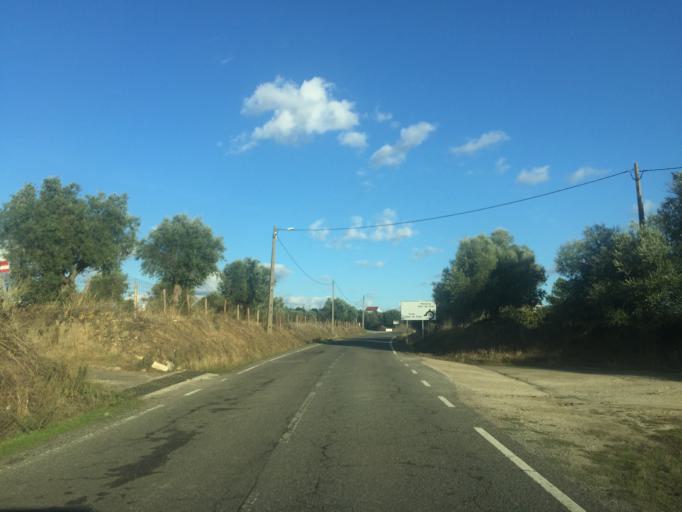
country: PT
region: Portalegre
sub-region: Alter do Chao
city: Alter do Chao
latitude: 39.1965
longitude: -7.6721
